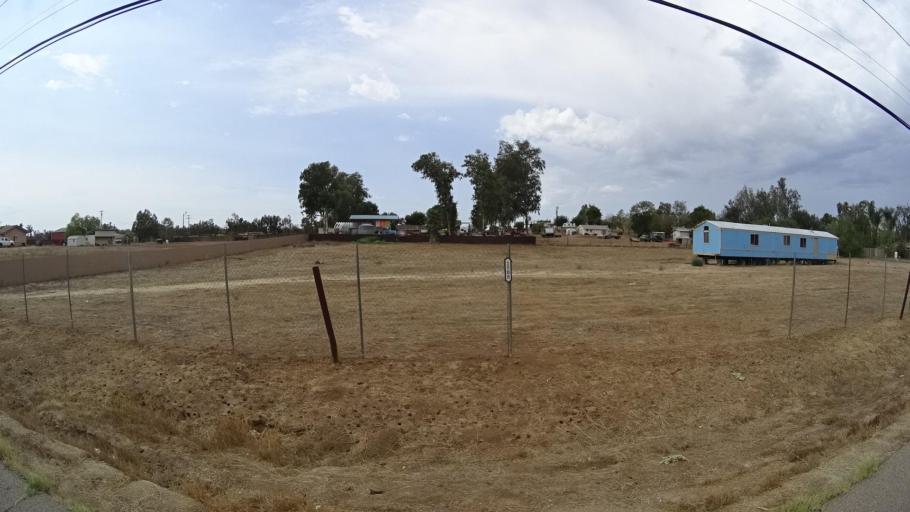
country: US
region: California
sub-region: San Diego County
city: Ramona
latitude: 33.0679
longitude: -116.8589
